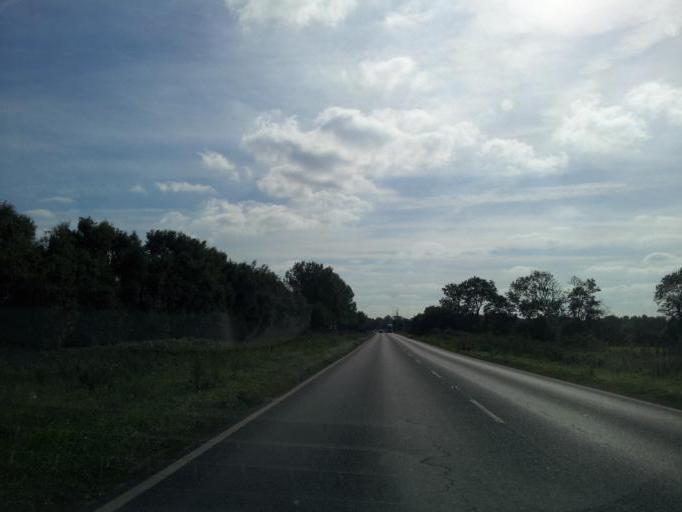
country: GB
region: England
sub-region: Cambridgeshire
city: Waterbeach
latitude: 52.2748
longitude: 0.1754
